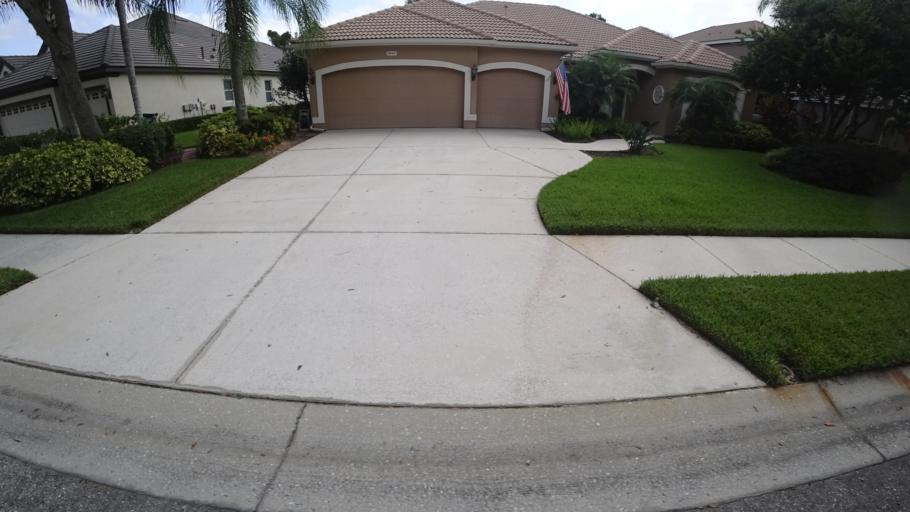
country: US
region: Florida
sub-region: Sarasota County
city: The Meadows
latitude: 27.4012
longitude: -82.4438
